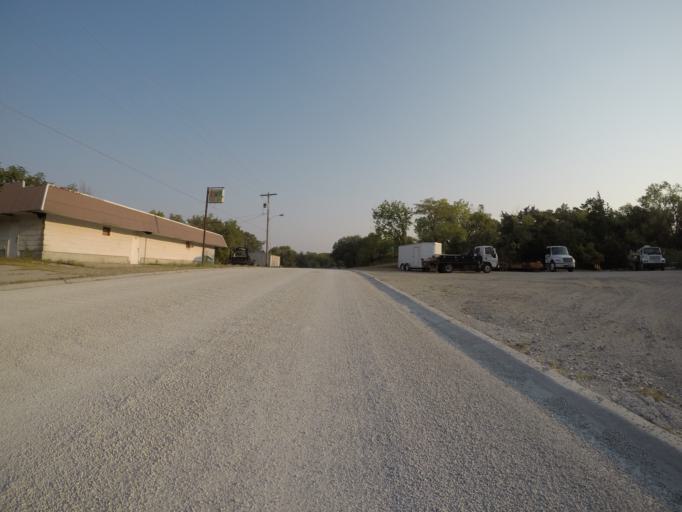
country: US
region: Kansas
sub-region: Marshall County
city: Marysville
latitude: 39.8477
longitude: -96.6481
